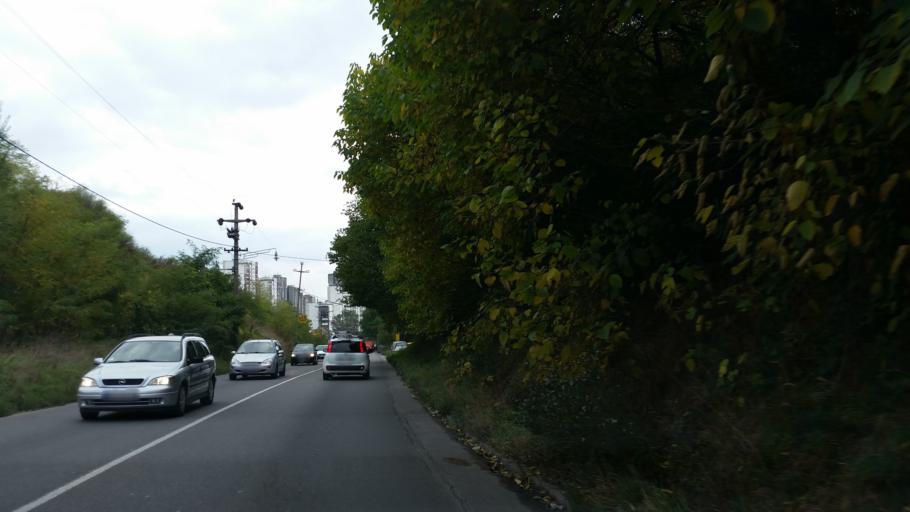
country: RS
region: Central Serbia
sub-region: Belgrade
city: Zemun
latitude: 44.8058
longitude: 20.3642
